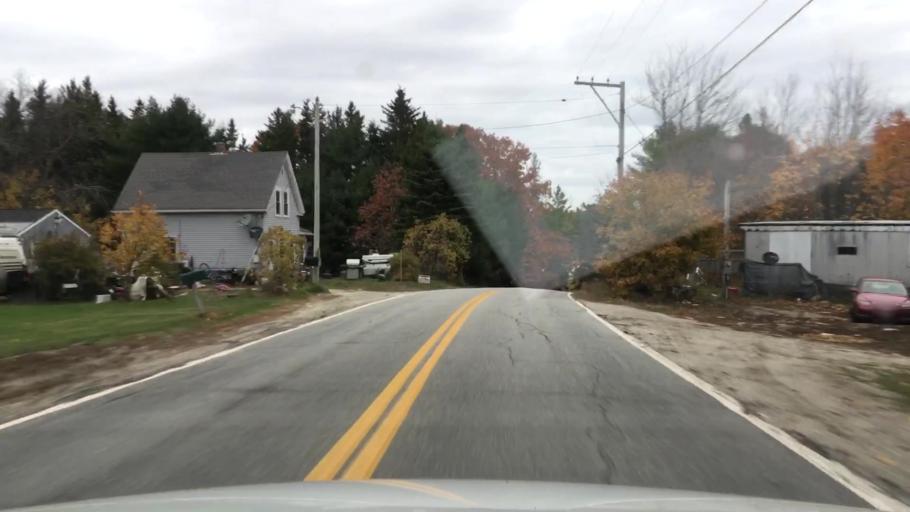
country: US
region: Maine
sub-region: Hancock County
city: Sedgwick
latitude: 44.3261
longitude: -68.5703
